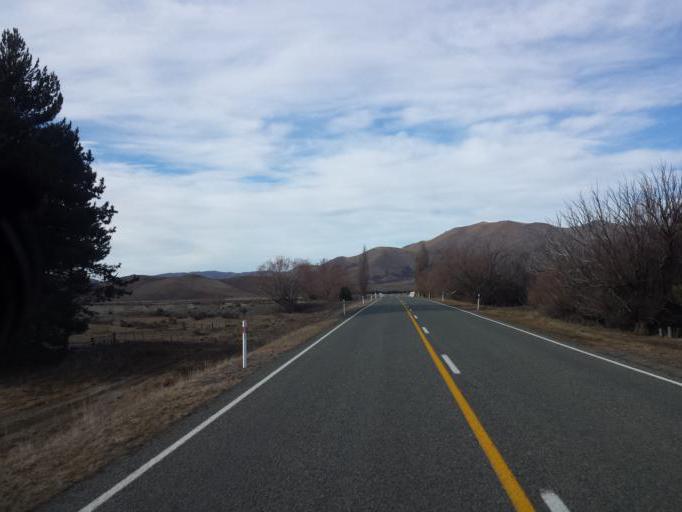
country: NZ
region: Canterbury
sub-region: Timaru District
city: Pleasant Point
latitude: -44.0874
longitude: 170.5455
